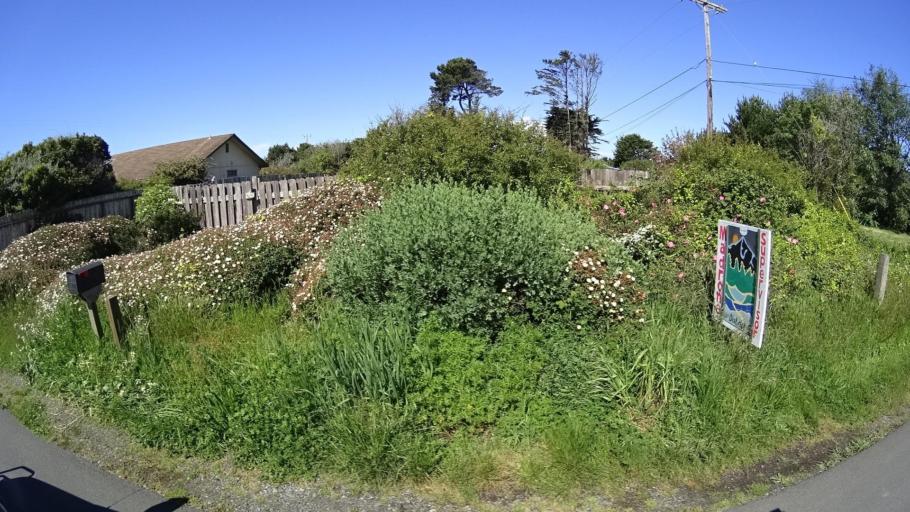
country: US
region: California
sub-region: Humboldt County
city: McKinleyville
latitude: 40.9355
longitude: -124.1265
